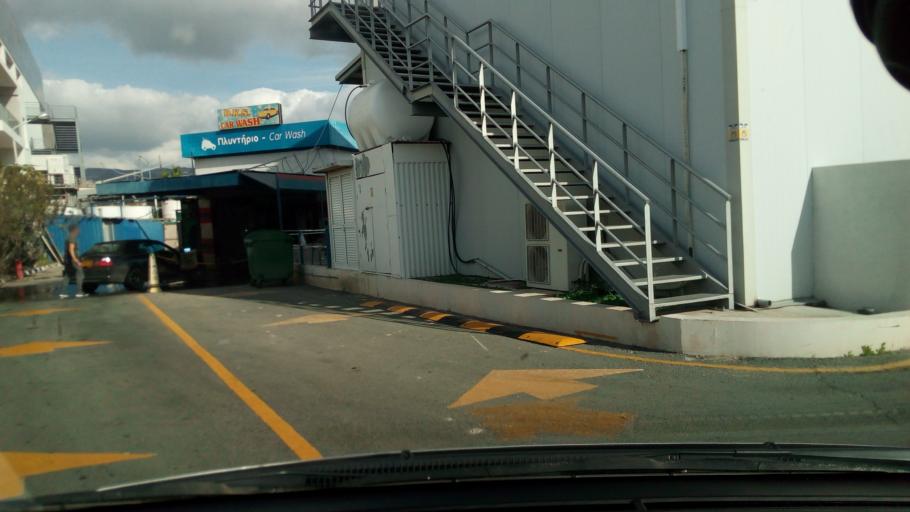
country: CY
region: Pafos
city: Paphos
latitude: 34.7816
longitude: 32.4438
